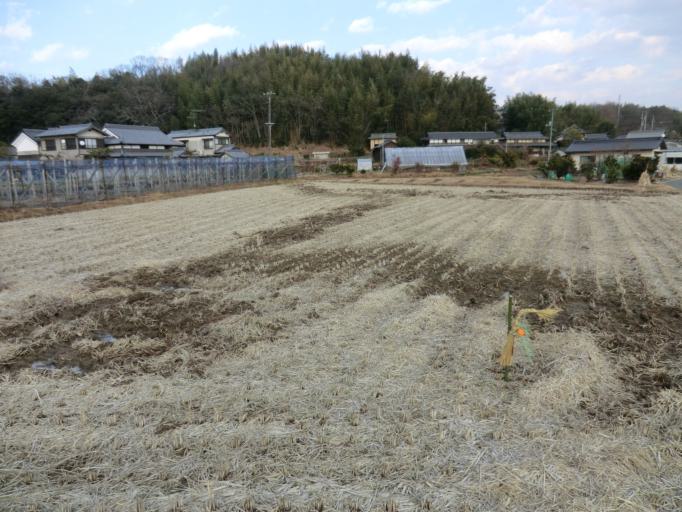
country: JP
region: Okayama
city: Okayama-shi
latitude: 34.7418
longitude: 134.0028
